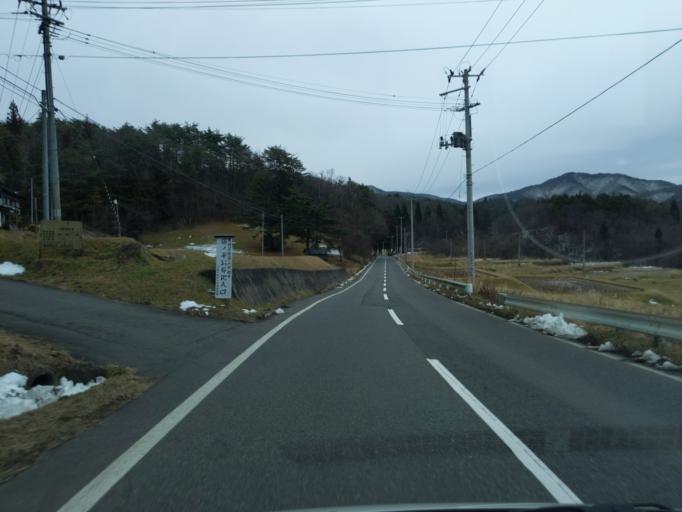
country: JP
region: Iwate
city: Mizusawa
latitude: 39.1158
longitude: 141.2630
